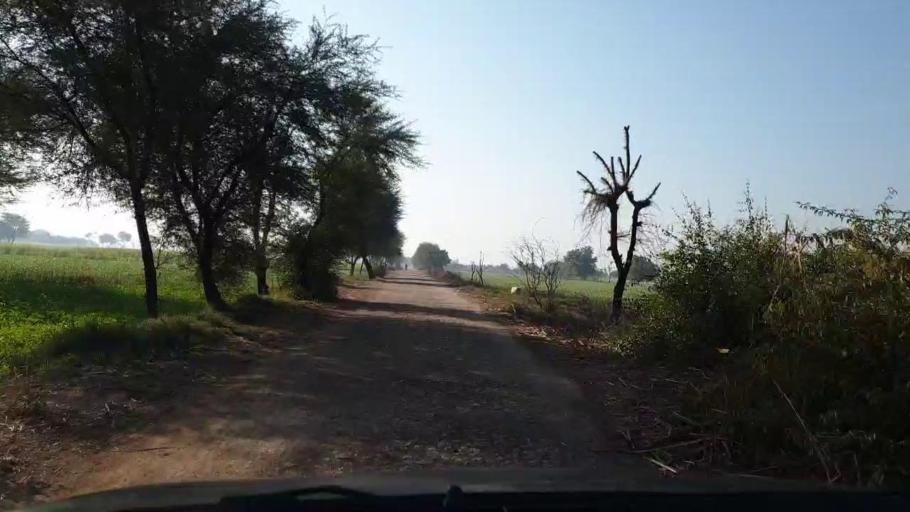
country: PK
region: Sindh
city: Jhol
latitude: 25.9365
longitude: 68.8654
